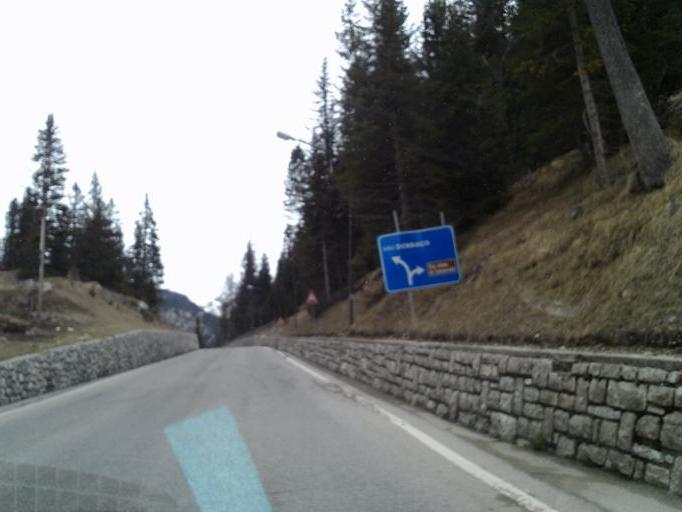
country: IT
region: Veneto
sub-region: Provincia di Belluno
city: Cortina d'Ampezzo
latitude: 46.5846
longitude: 12.2541
